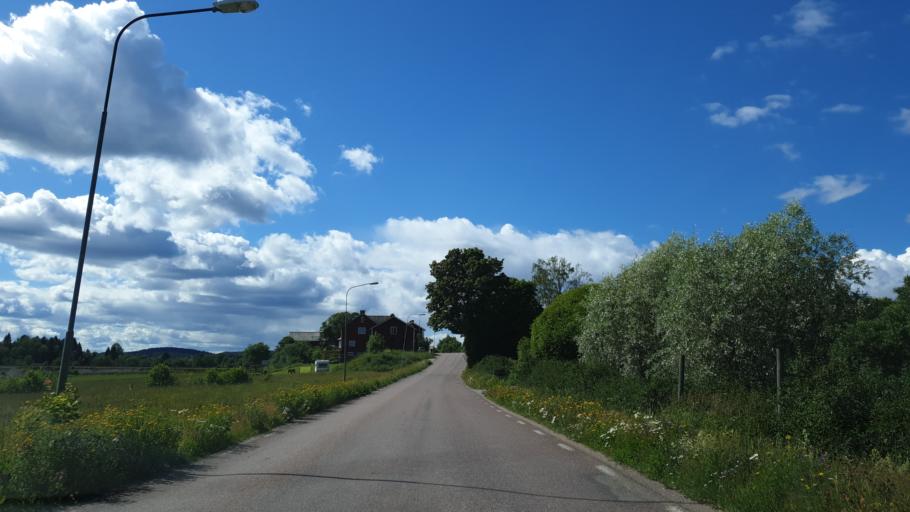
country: SE
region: Gaevleborg
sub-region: Nordanstigs Kommun
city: Bergsjoe
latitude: 62.0494
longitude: 17.2290
